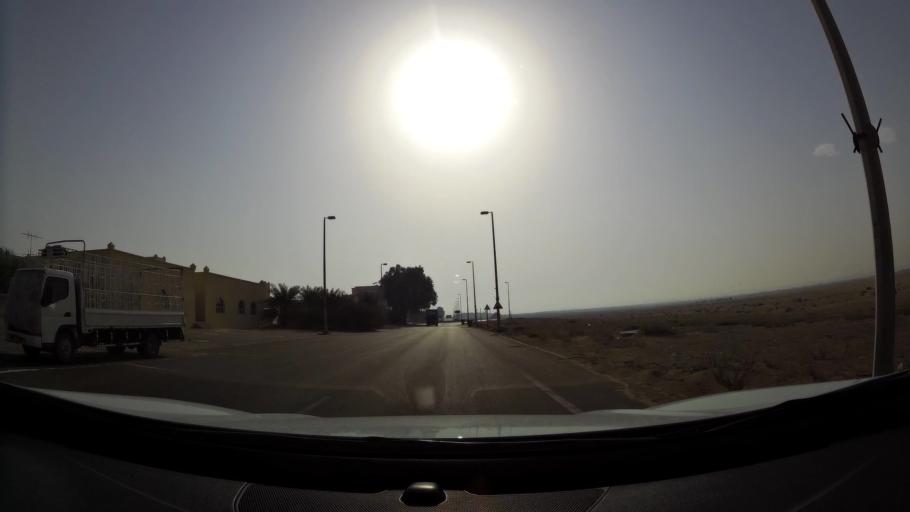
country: AE
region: Abu Dhabi
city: Abu Dhabi
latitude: 24.2620
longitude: 54.6638
